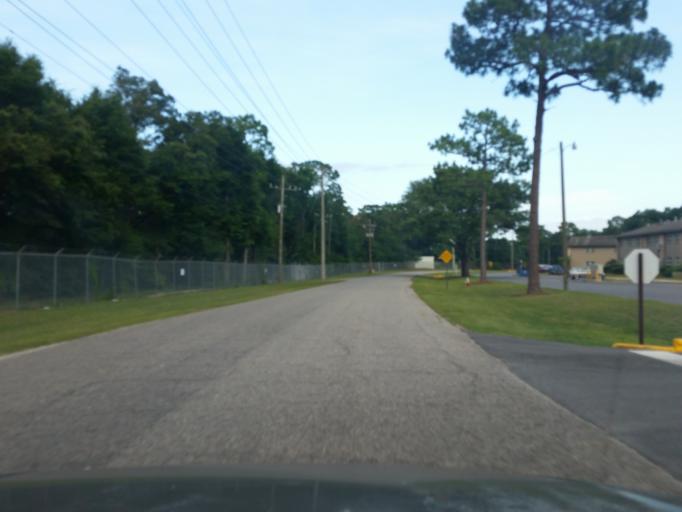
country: US
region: Florida
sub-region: Escambia County
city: Ferry Pass
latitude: 30.5161
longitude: -87.1725
